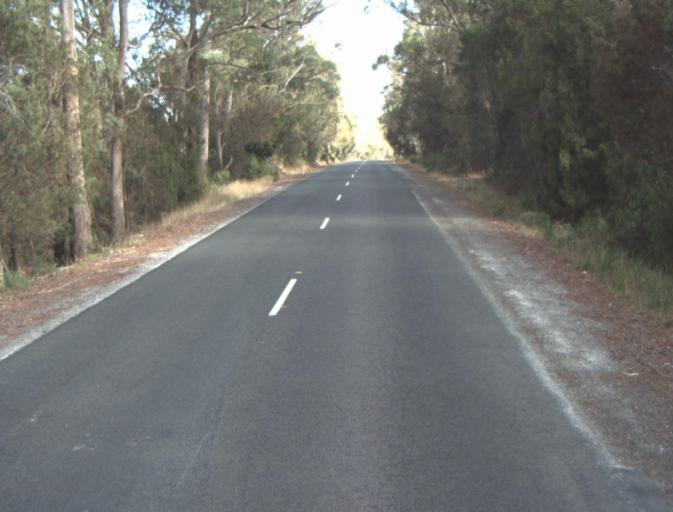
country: AU
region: Tasmania
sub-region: Dorset
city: Bridport
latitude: -41.1218
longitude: 147.2059
